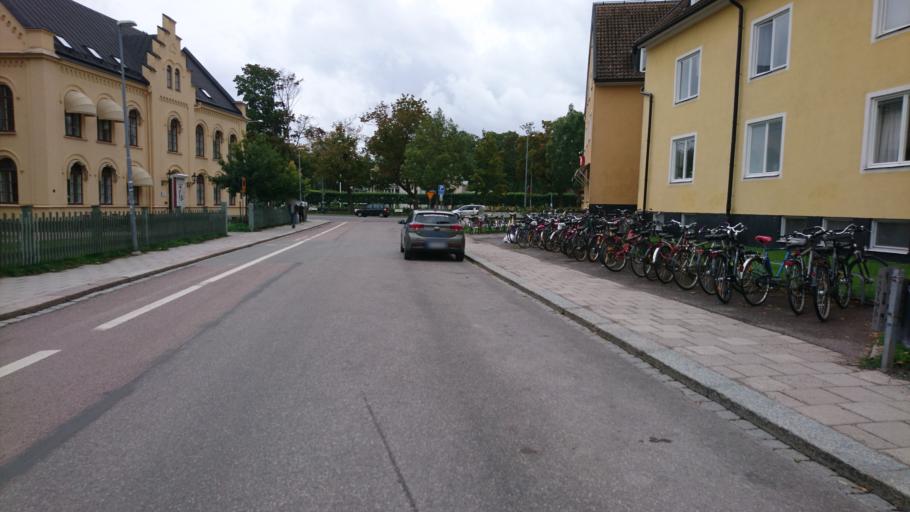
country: SE
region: Uppsala
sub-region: Uppsala Kommun
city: Uppsala
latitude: 59.8549
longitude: 17.6393
